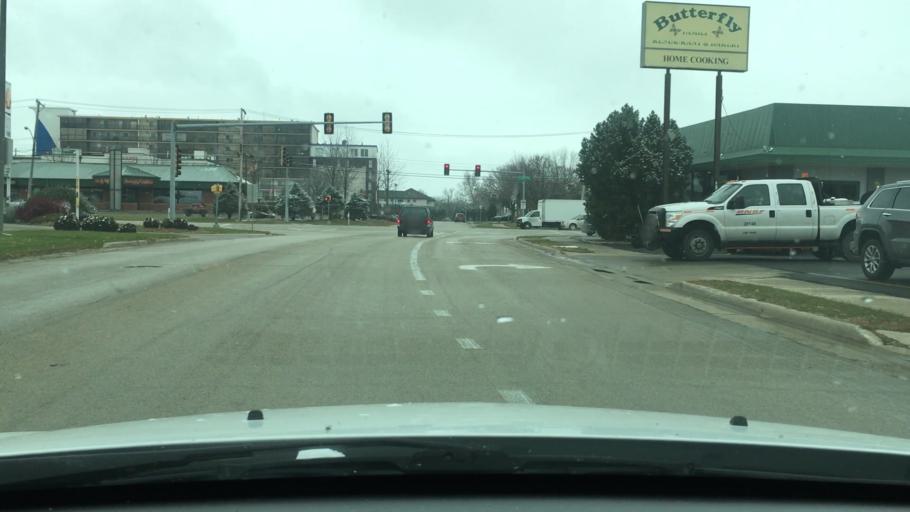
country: US
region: Illinois
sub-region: Ogle County
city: Rochelle
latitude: 41.9333
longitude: -89.0665
